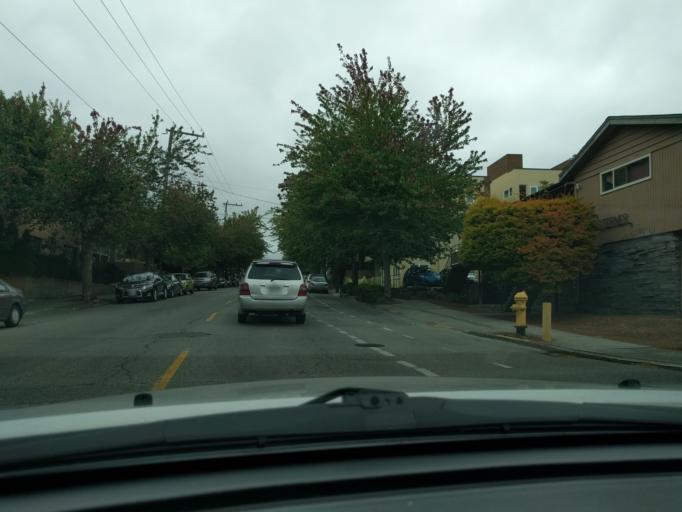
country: US
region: Washington
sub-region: King County
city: Seattle
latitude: 47.6577
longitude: -122.3500
